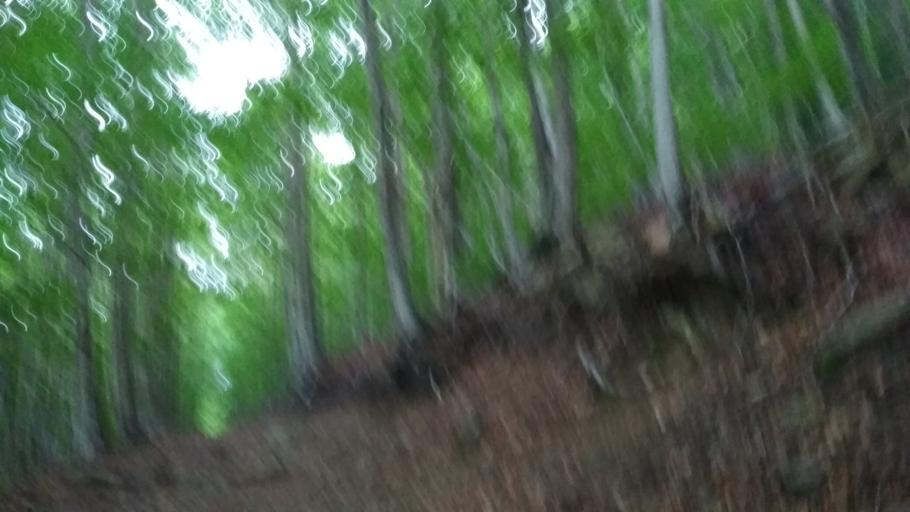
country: ES
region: Catalonia
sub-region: Provincia de Barcelona
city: Fogars de Montclus
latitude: 41.7778
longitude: 2.4498
